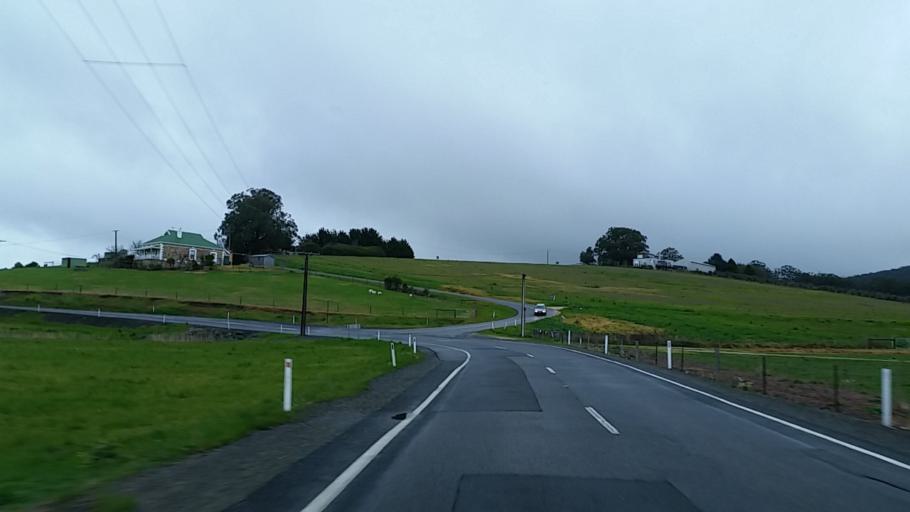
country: AU
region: South Australia
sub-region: Adelaide Hills
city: Bridgewater
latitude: -34.9661
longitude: 138.7344
